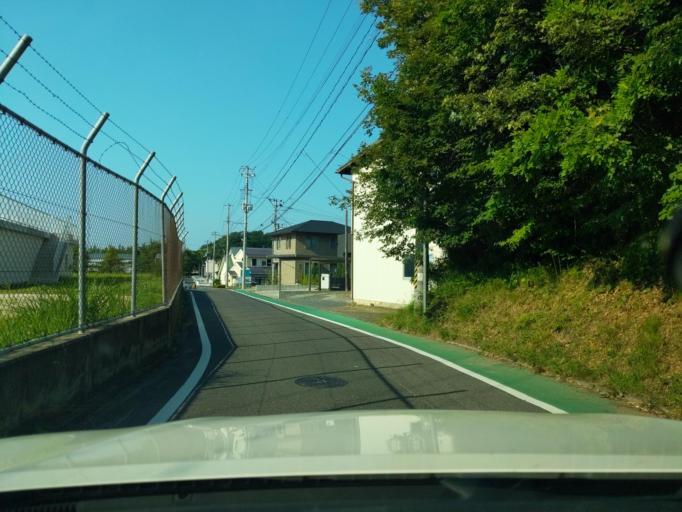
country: JP
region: Fukushima
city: Sukagawa
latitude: 37.2823
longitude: 140.3548
